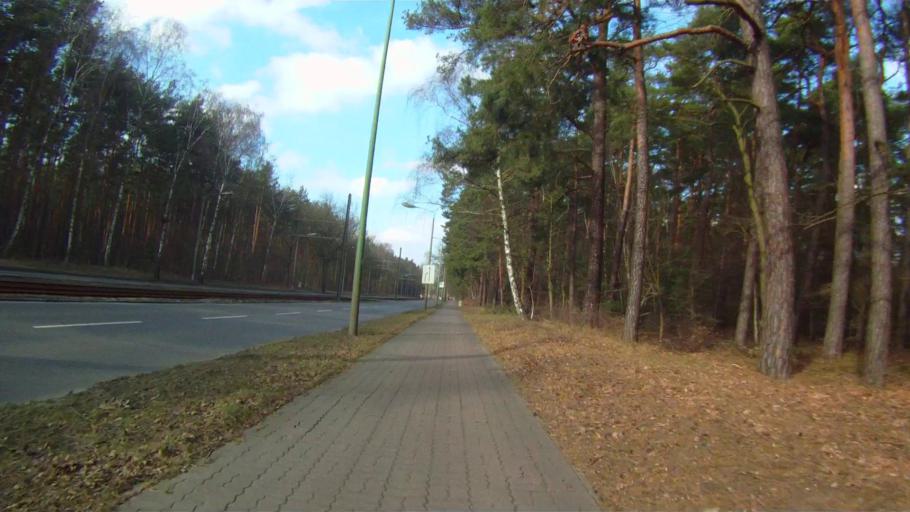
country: DE
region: Berlin
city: Schmockwitz
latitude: 52.3830
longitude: 13.6388
